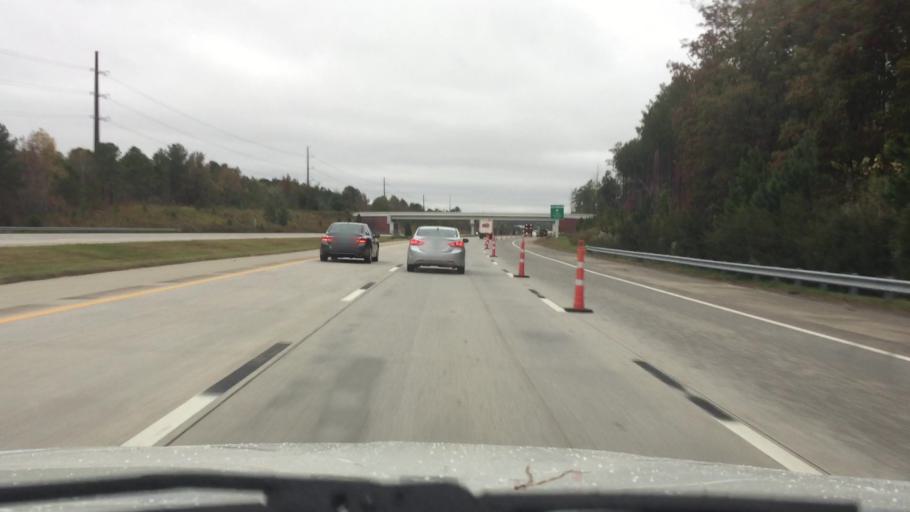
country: US
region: North Carolina
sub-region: Wake County
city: Green Level
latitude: 35.8061
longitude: -78.8918
